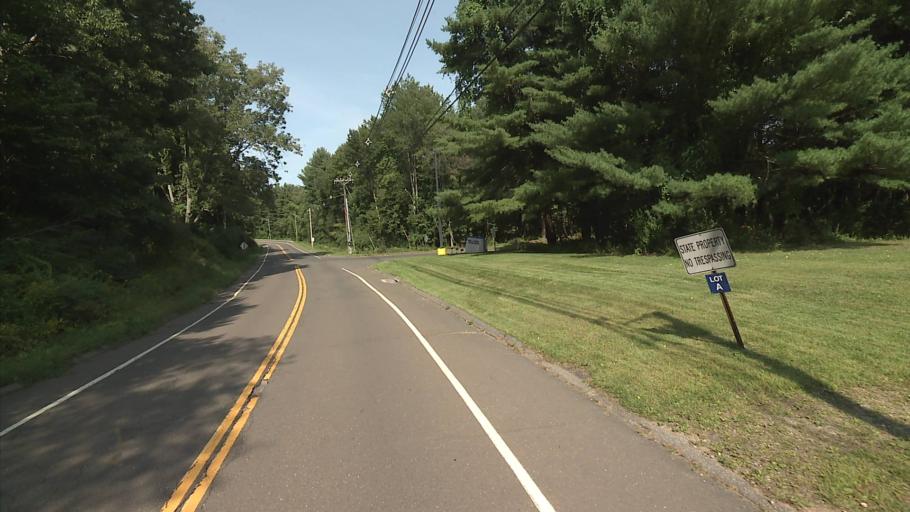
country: US
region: Connecticut
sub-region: Fairfield County
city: Newtown
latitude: 41.3982
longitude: -73.2749
